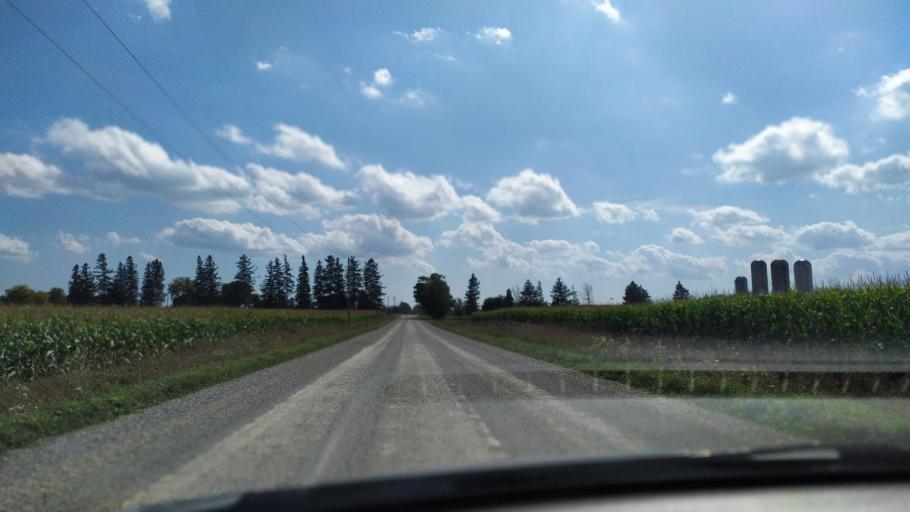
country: CA
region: Ontario
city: Stratford
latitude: 43.2740
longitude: -80.9233
